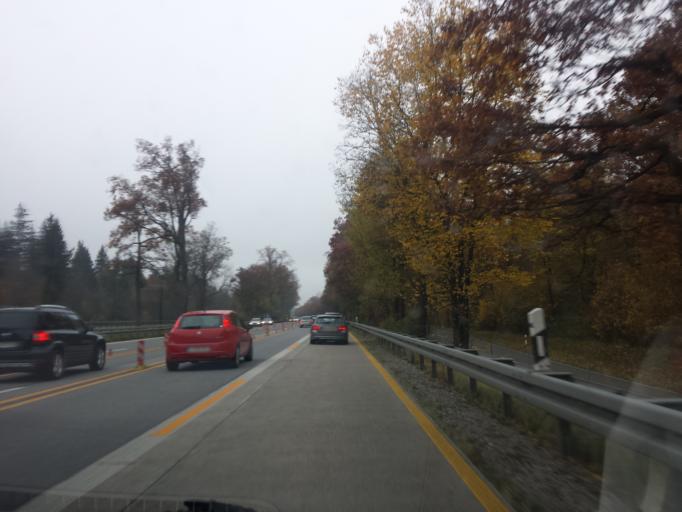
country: DE
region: Bavaria
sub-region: Upper Bavaria
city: Neuried
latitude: 48.0535
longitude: 11.4575
